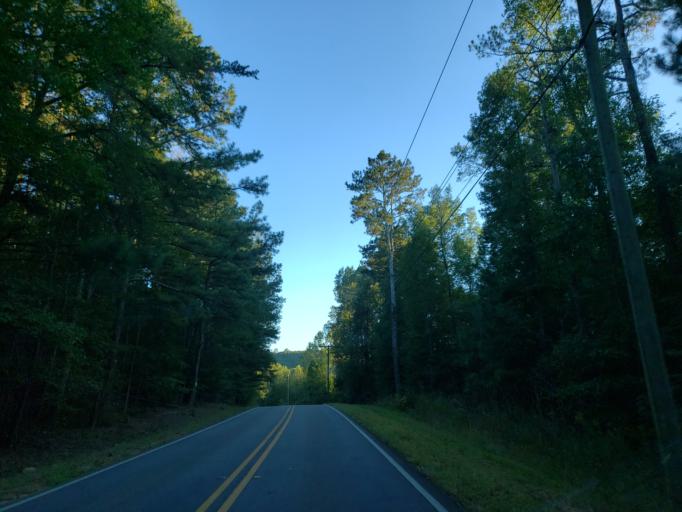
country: US
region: Georgia
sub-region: Bartow County
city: Rydal
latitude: 34.3768
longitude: -84.5895
